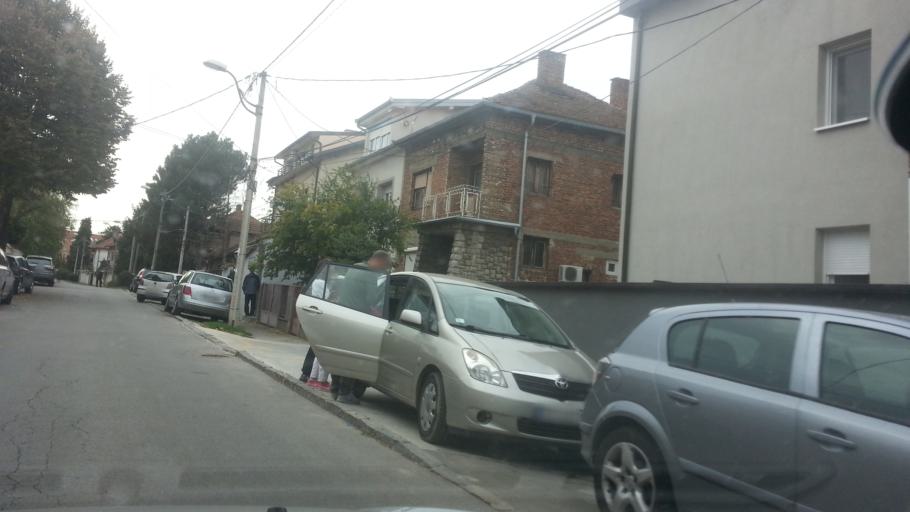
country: RS
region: Central Serbia
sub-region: Belgrade
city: Zemun
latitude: 44.8377
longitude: 20.3994
